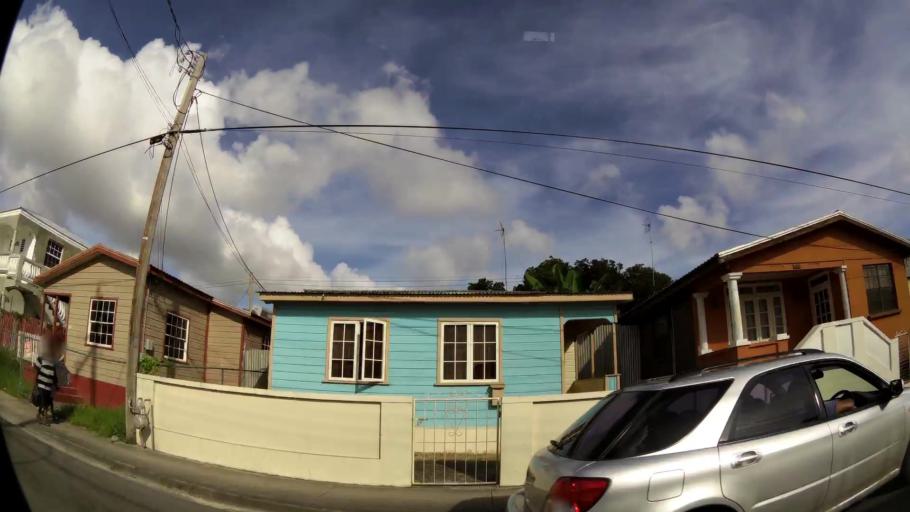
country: BB
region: Saint Michael
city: Bridgetown
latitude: 13.0899
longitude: -59.6015
